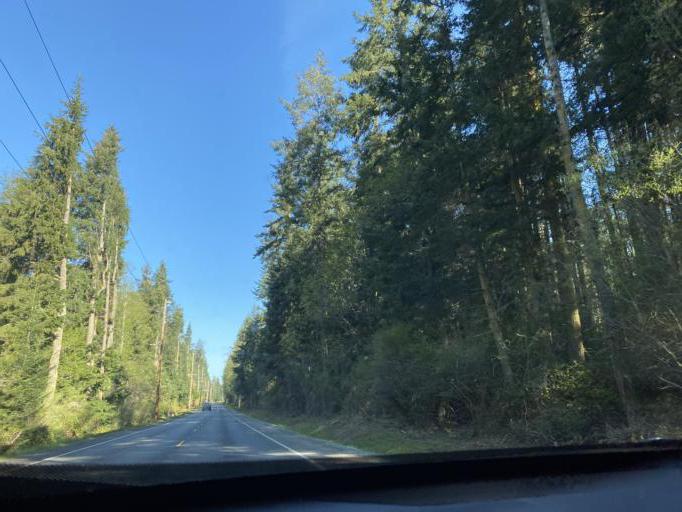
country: US
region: Washington
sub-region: Island County
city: Freeland
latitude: 48.0652
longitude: -122.5986
